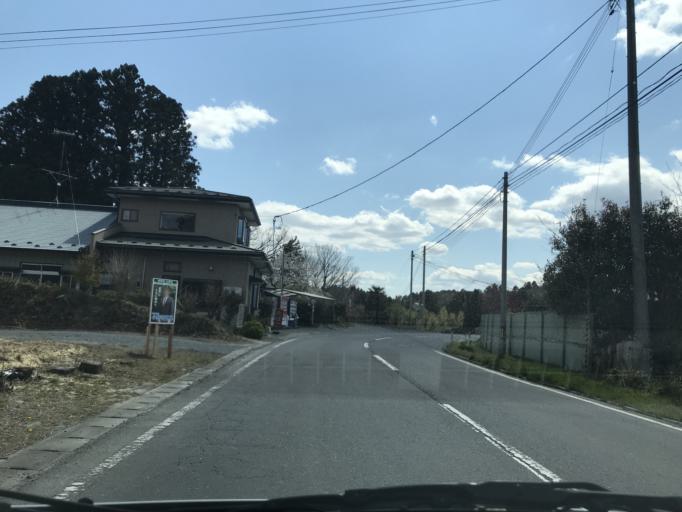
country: JP
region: Miyagi
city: Wakuya
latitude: 38.6382
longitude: 141.2304
